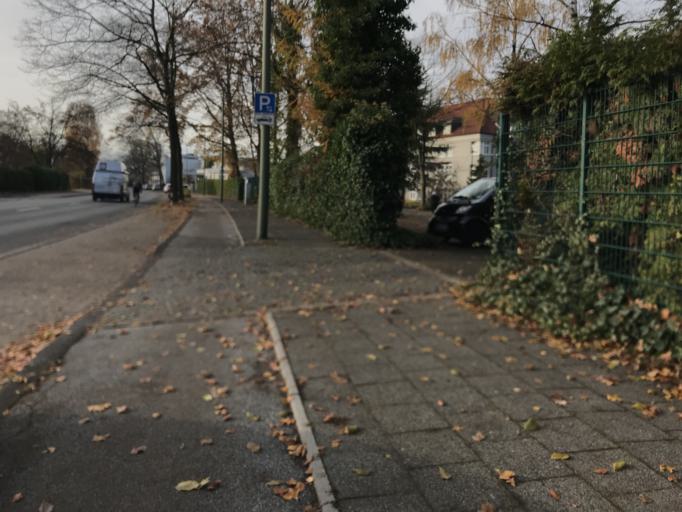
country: DE
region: North Rhine-Westphalia
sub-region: Regierungsbezirk Arnsberg
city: Hamm
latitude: 51.6886
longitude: 7.8525
